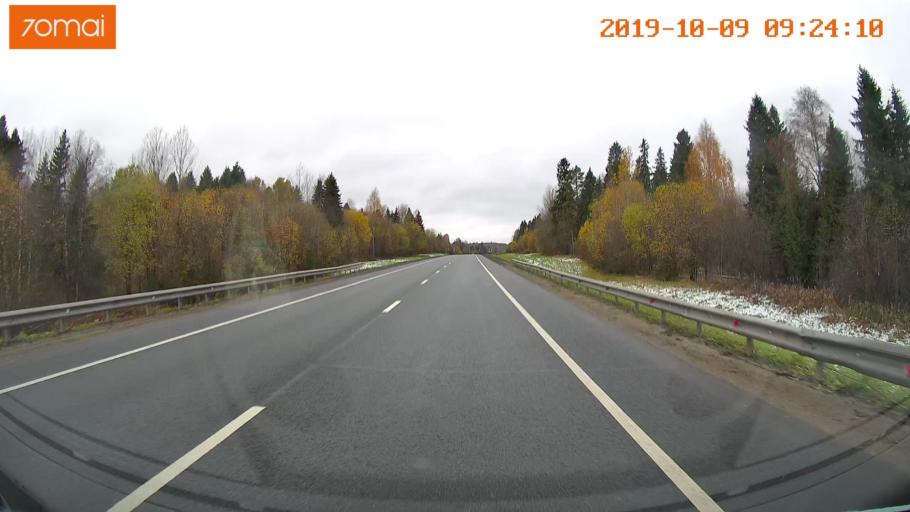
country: RU
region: Vologda
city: Vologda
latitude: 59.0761
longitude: 40.0204
